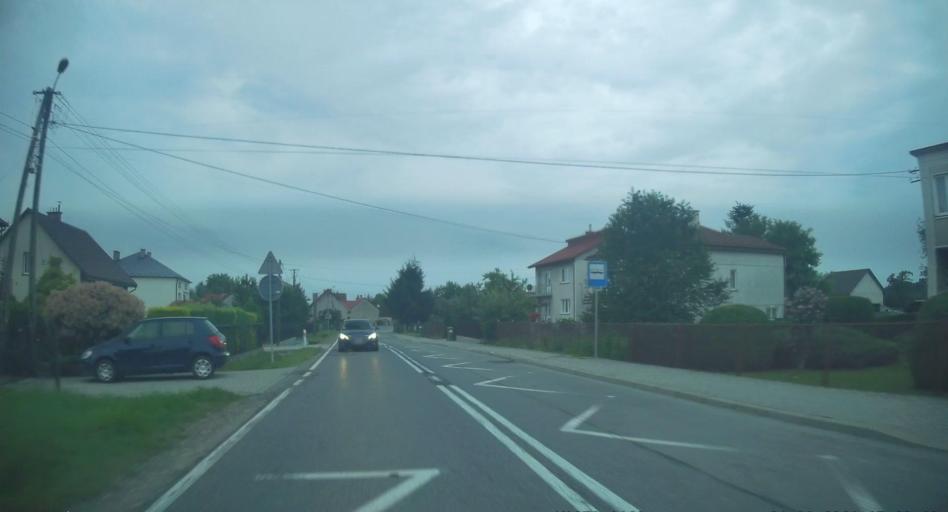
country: PL
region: Lesser Poland Voivodeship
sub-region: Powiat tarnowski
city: Wierzchoslawice
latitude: 49.9975
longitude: 20.8537
